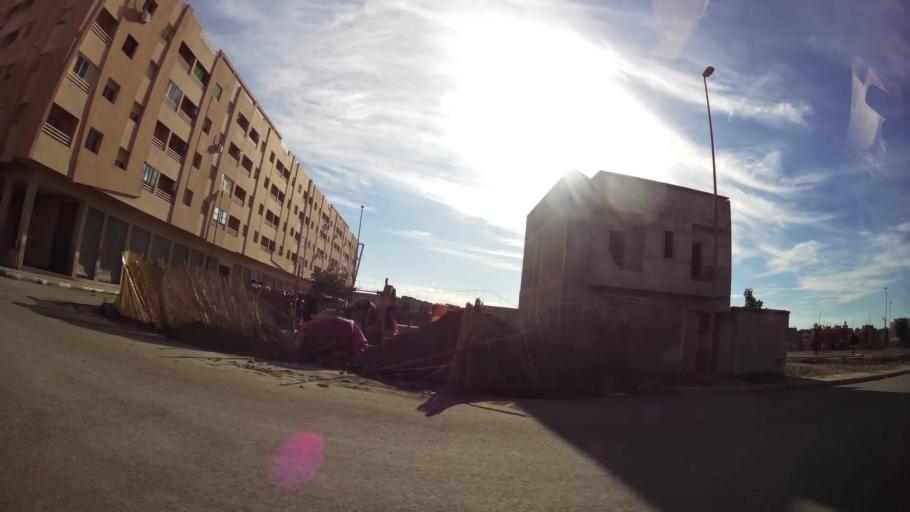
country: MA
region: Marrakech-Tensift-Al Haouz
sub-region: Marrakech
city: Marrakesh
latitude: 31.6873
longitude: -8.0643
